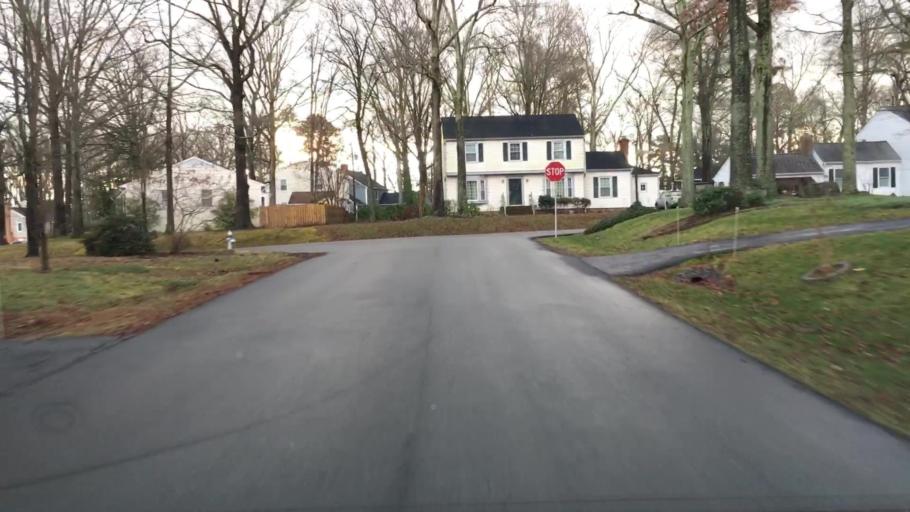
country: US
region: Virginia
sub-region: Chesterfield County
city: Bon Air
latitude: 37.5168
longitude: -77.6206
